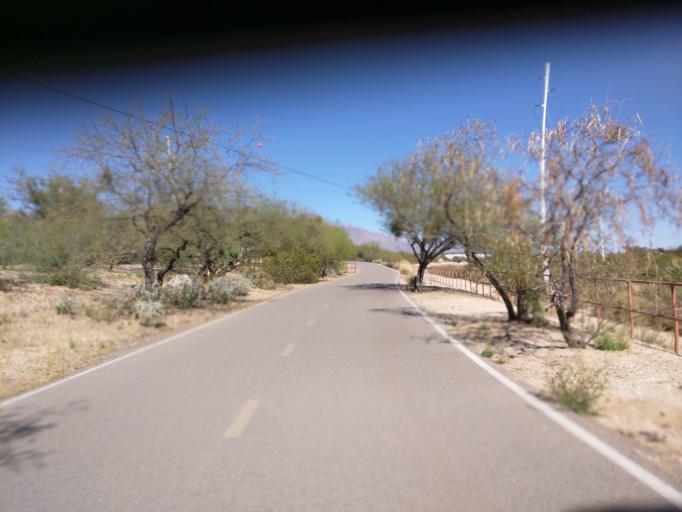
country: US
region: Arizona
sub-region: Pima County
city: Flowing Wells
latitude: 32.2938
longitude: -110.9875
